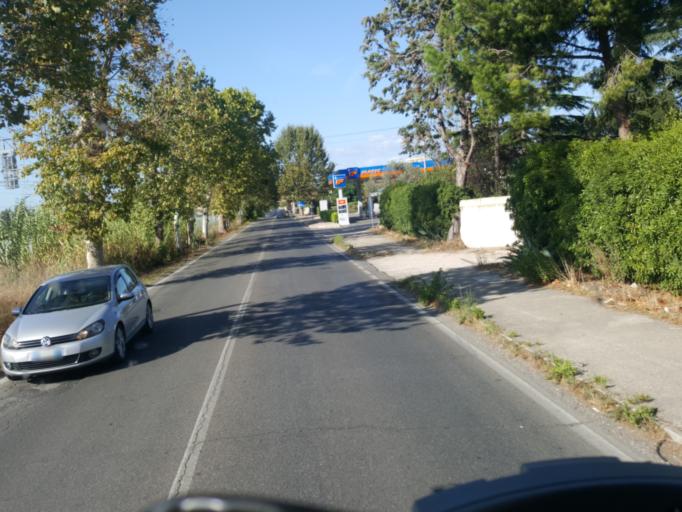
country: IT
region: Latium
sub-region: Provincia di Latina
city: Campo di Carne
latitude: 41.5490
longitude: 12.6352
